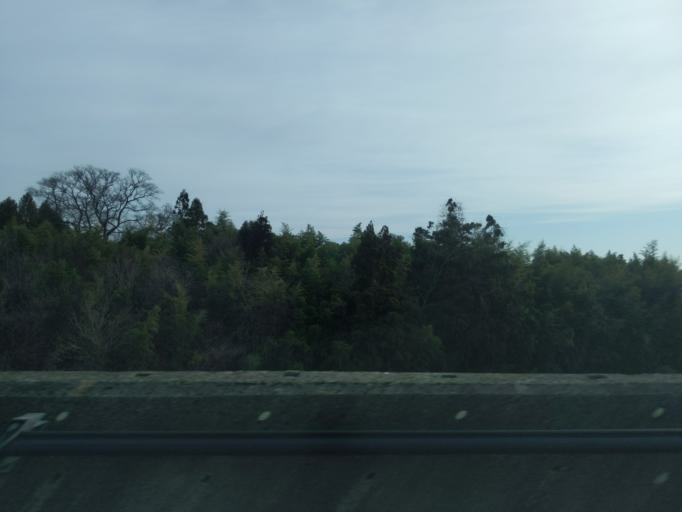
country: JP
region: Iwate
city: Ichinoseki
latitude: 38.7658
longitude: 141.0813
